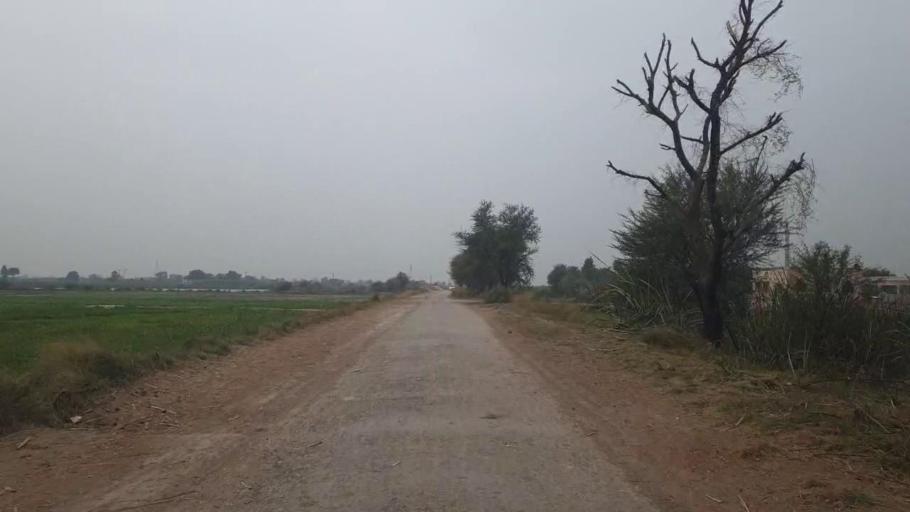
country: PK
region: Sindh
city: Shahdadpur
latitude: 25.8667
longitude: 68.6282
